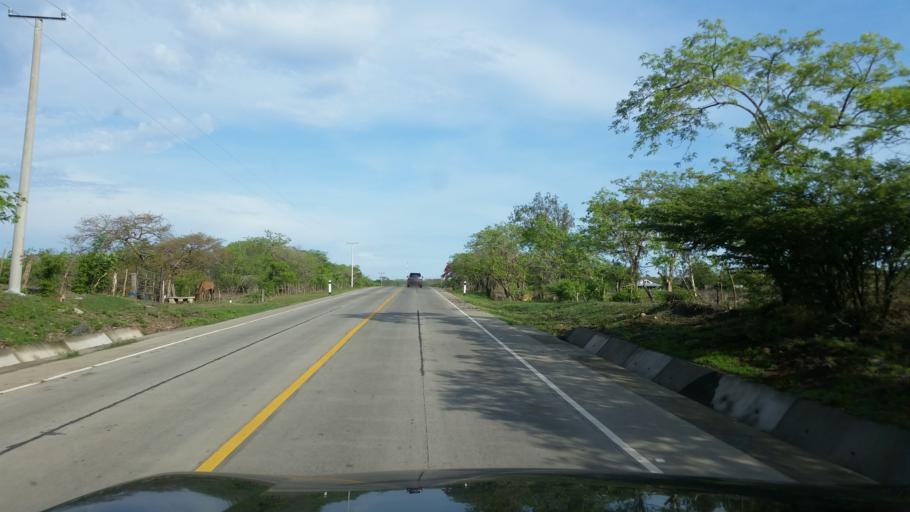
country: NI
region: Leon
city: Nagarote
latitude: 12.1122
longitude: -86.6033
